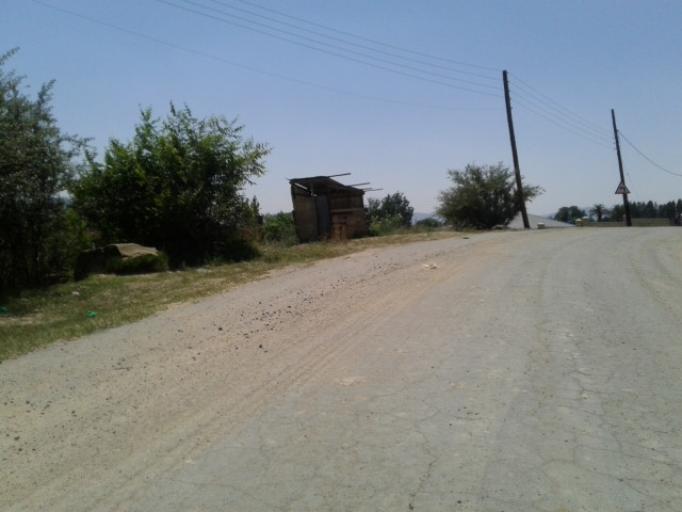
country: LS
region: Maseru
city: Maseru
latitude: -29.3046
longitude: 27.4749
